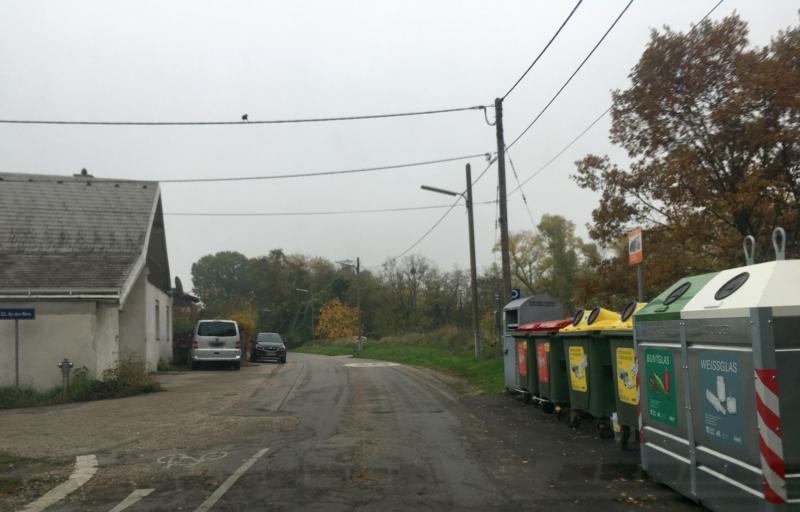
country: AT
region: Lower Austria
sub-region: Politischer Bezirk Ganserndorf
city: Gross-Enzersdorf
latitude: 48.2051
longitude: 16.4783
